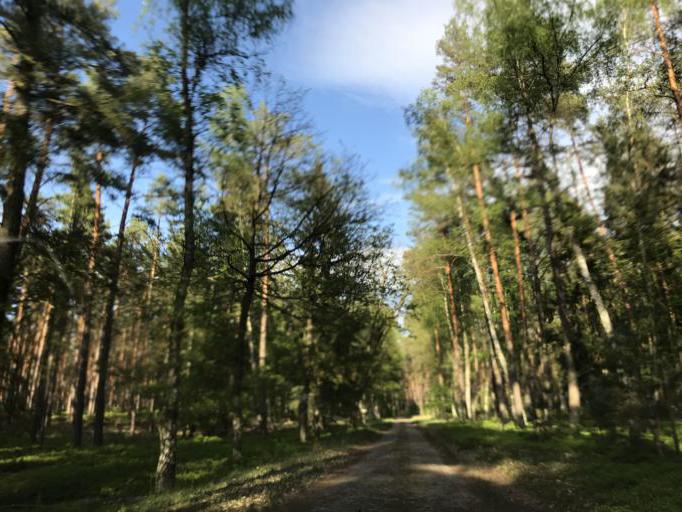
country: DE
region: Brandenburg
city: Joachimsthal
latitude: 52.9592
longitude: 13.6806
